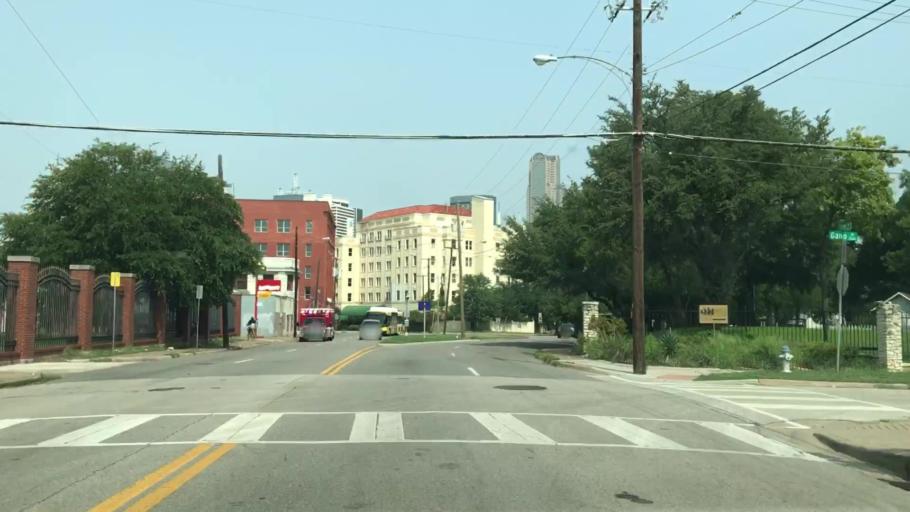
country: US
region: Texas
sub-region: Dallas County
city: Dallas
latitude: 32.7714
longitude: -96.7891
